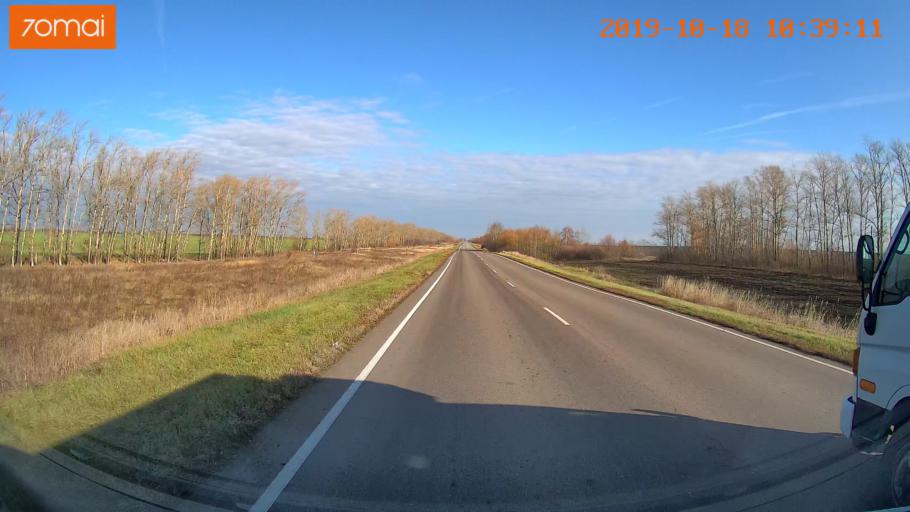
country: RU
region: Tula
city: Kurkino
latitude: 53.5833
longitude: 38.6499
